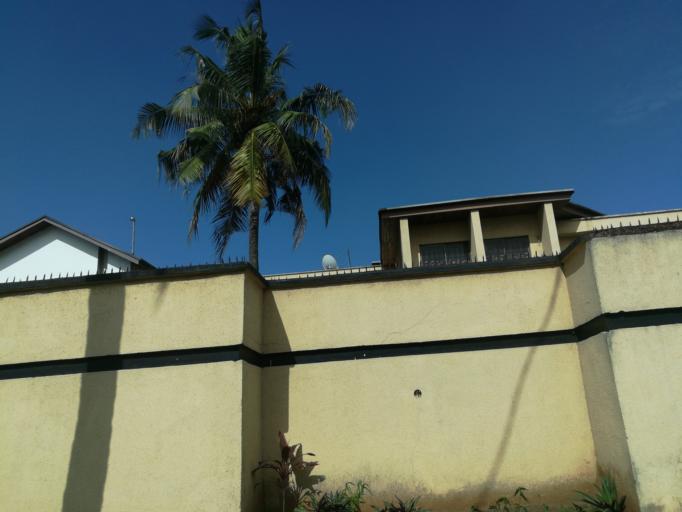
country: NG
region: Lagos
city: Ojota
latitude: 6.5760
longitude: 3.3639
